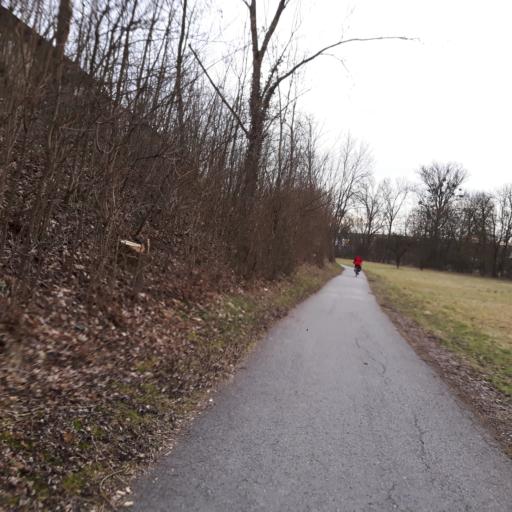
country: DE
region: Baden-Wuerttemberg
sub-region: Regierungsbezirk Stuttgart
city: Grossbottwar
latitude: 48.9842
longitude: 9.2889
